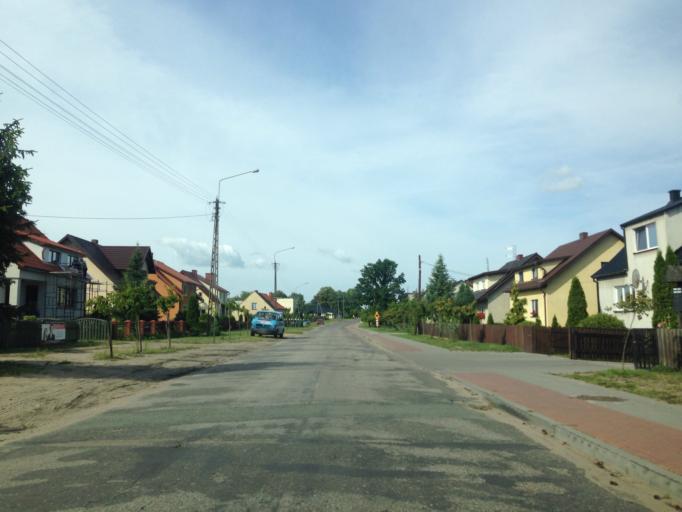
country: PL
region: Kujawsko-Pomorskie
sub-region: Powiat tucholski
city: Sliwice
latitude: 53.7160
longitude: 18.1857
